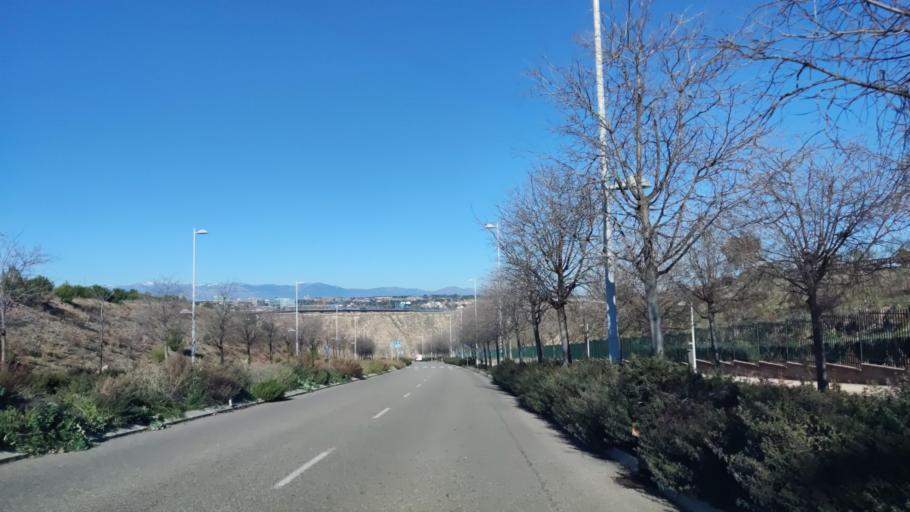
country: ES
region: Madrid
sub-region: Provincia de Madrid
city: Hortaleza
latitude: 40.4904
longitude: -3.6423
